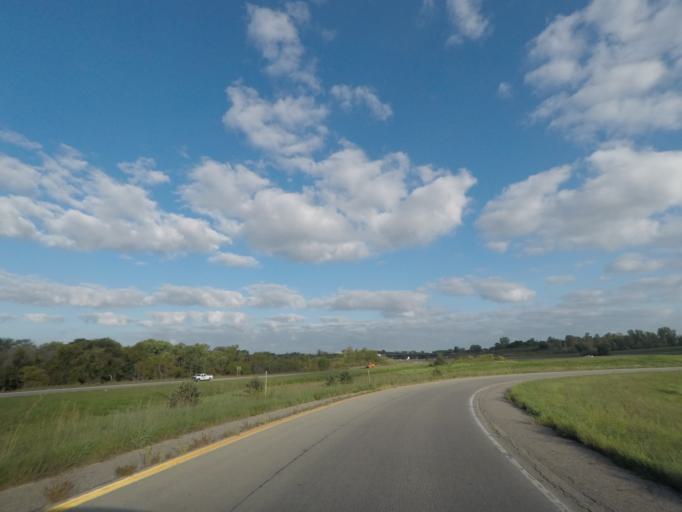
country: US
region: Iowa
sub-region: Warren County
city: Norwalk
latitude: 41.5065
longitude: -93.6469
